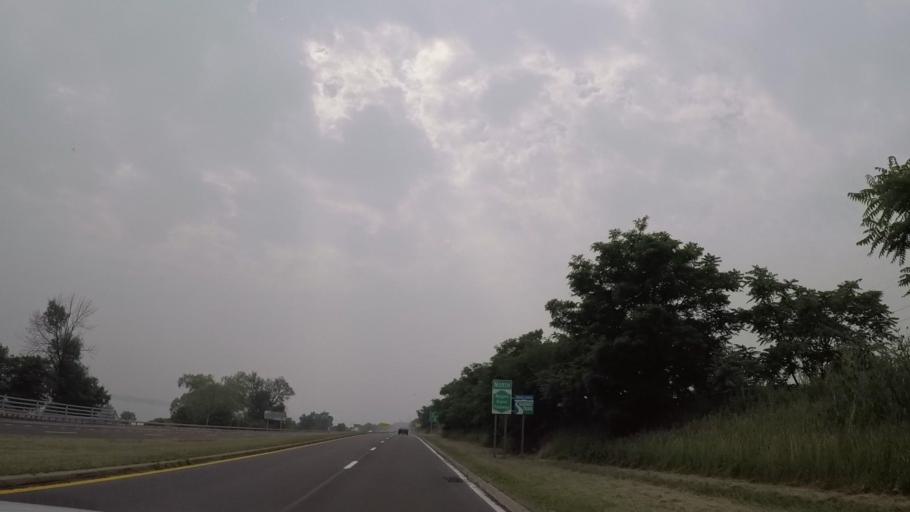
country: US
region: New York
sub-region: Niagara County
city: Niagara Falls
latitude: 43.0788
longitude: -79.0201
